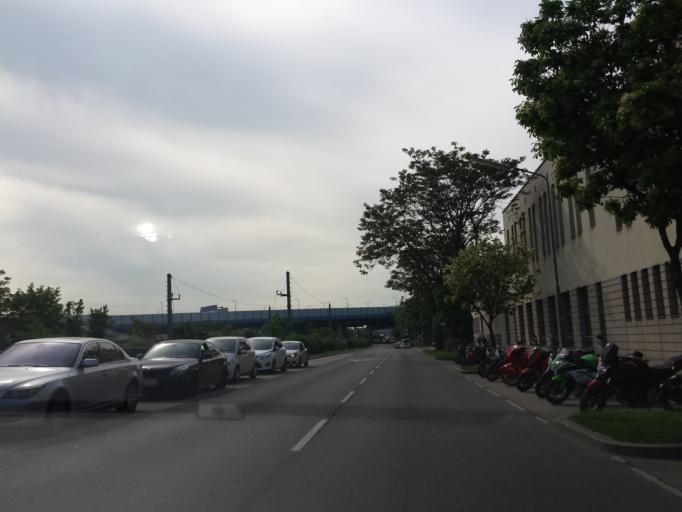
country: AT
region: Vienna
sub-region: Wien Stadt
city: Vienna
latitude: 48.1858
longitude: 16.4018
